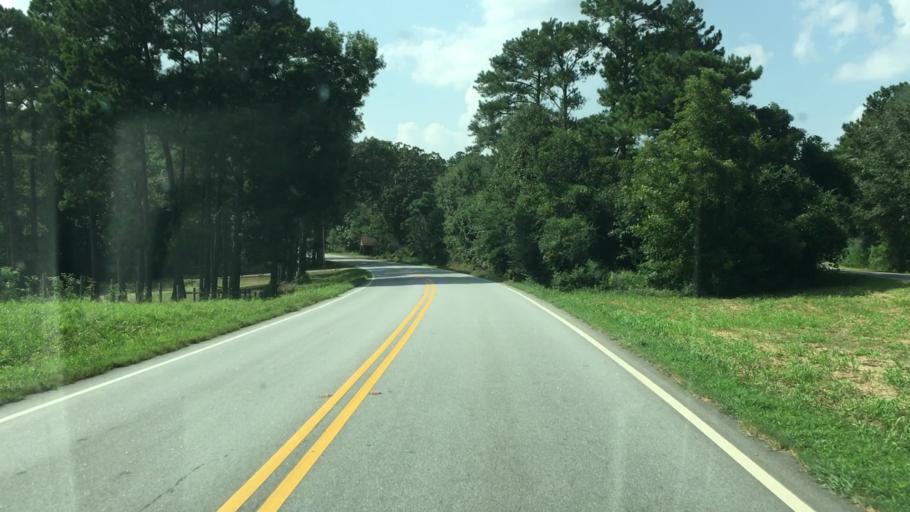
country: US
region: Georgia
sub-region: Jasper County
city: Monticello
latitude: 33.3522
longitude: -83.7226
